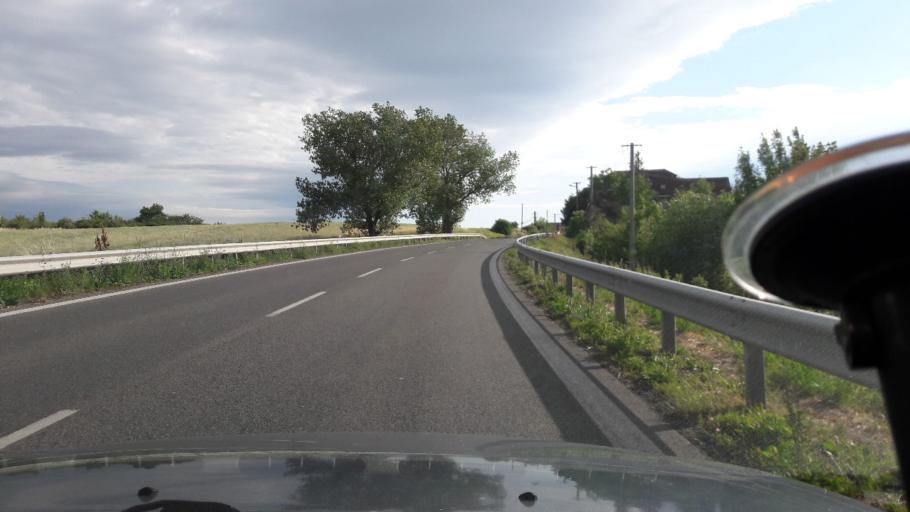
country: SK
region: Bratislavsky
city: Modra
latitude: 48.3095
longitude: 17.2935
